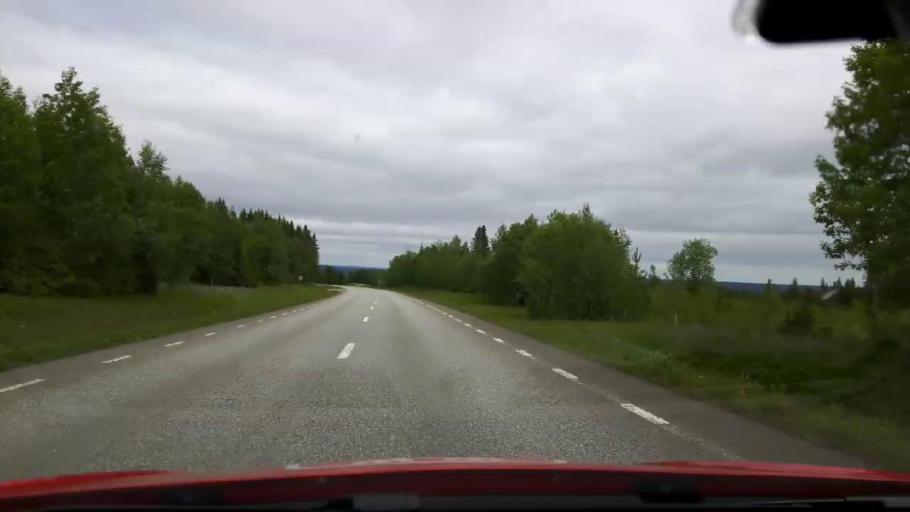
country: SE
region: Jaemtland
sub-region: Krokoms Kommun
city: Krokom
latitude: 63.5746
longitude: 14.6304
